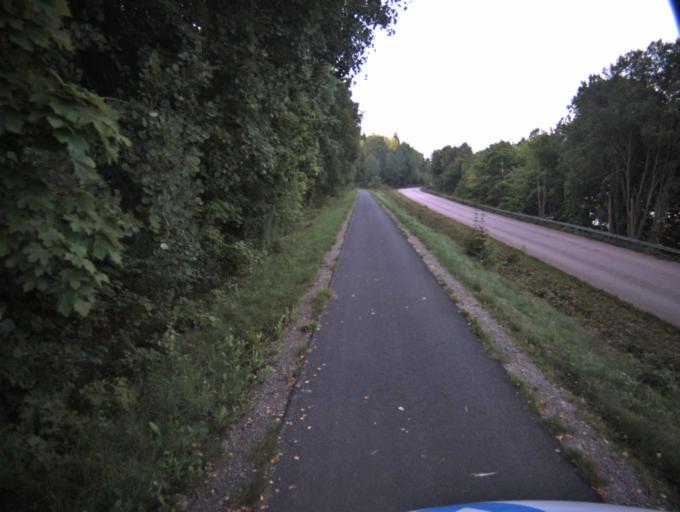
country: SE
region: Vaestra Goetaland
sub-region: Ulricehamns Kommun
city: Ulricehamn
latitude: 57.7627
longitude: 13.3993
